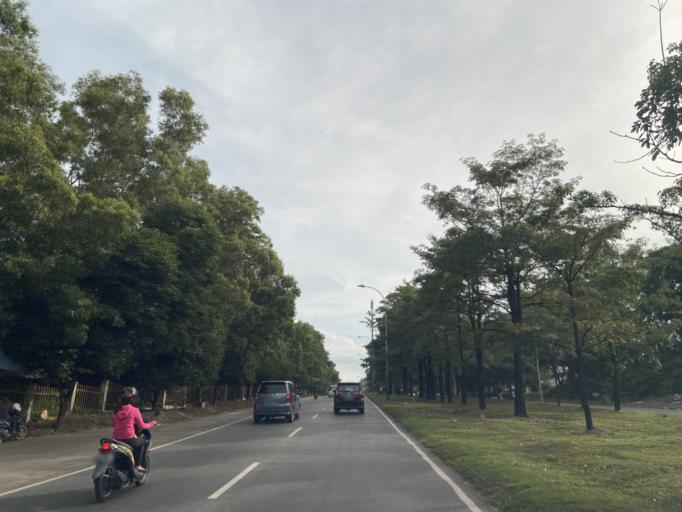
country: SG
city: Singapore
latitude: 1.1365
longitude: 104.0230
